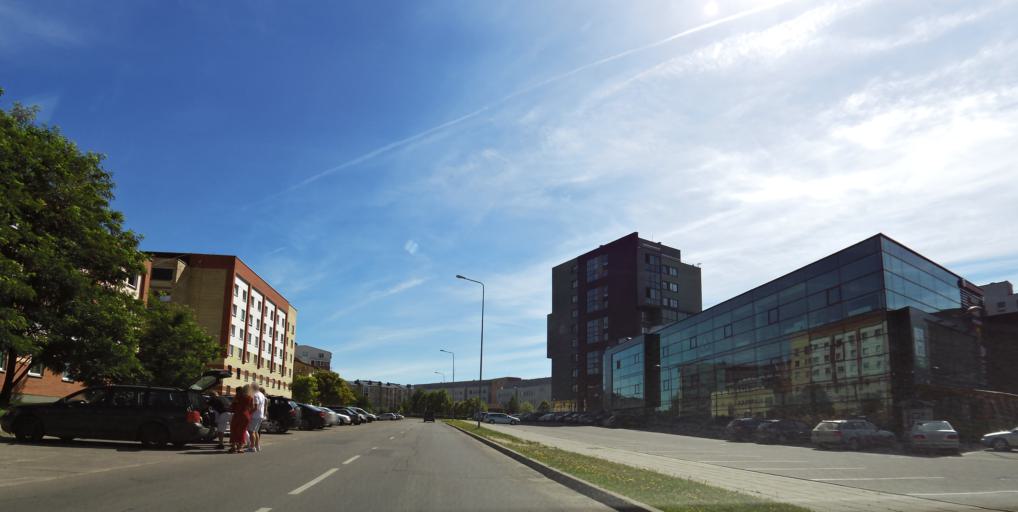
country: LT
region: Vilnius County
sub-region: Vilnius
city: Fabijoniskes
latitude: 54.7236
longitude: 25.2346
